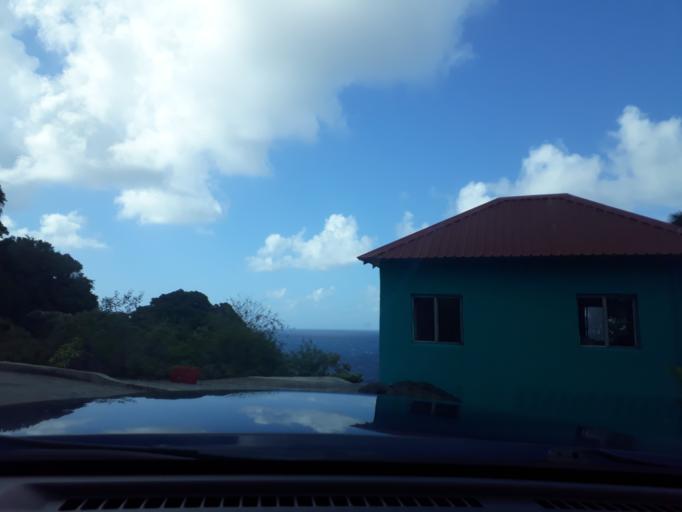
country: VC
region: Charlotte
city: Georgetown
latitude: 13.3806
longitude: -61.1730
